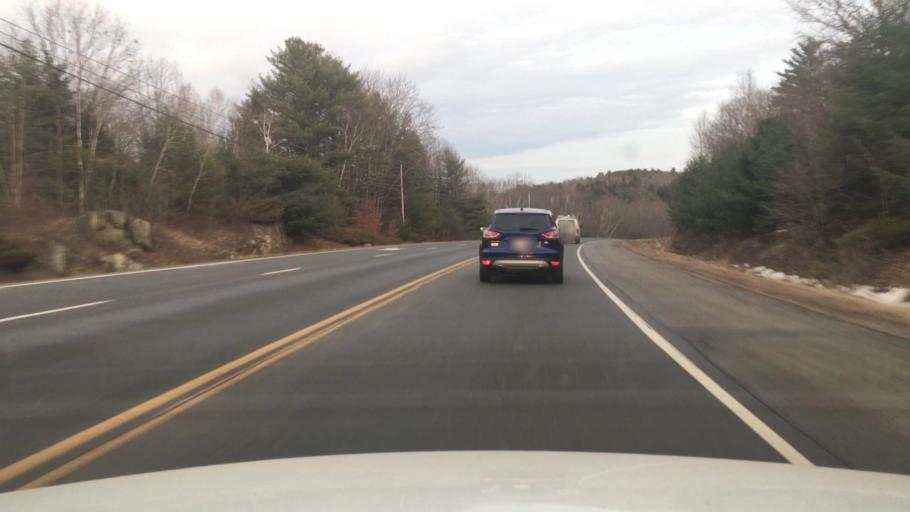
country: US
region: Maine
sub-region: Lincoln County
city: Edgecomb
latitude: 44.0102
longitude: -69.6027
